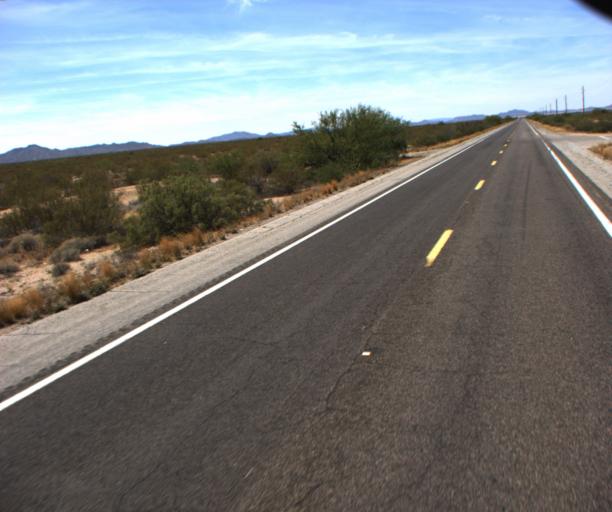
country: US
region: Arizona
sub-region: La Paz County
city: Salome
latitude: 33.8472
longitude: -113.4597
